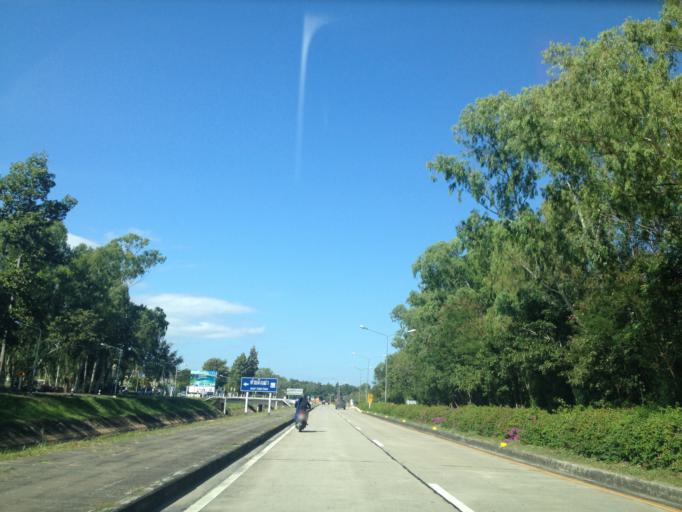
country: TH
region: Chiang Mai
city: Chiang Mai
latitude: 18.8586
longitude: 98.9616
